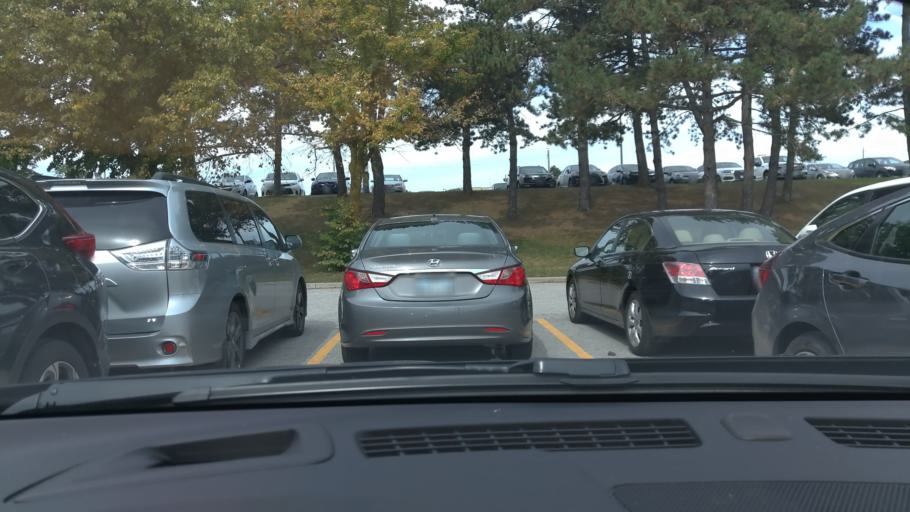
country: CA
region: Ontario
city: Willowdale
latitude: 43.7189
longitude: -79.3398
